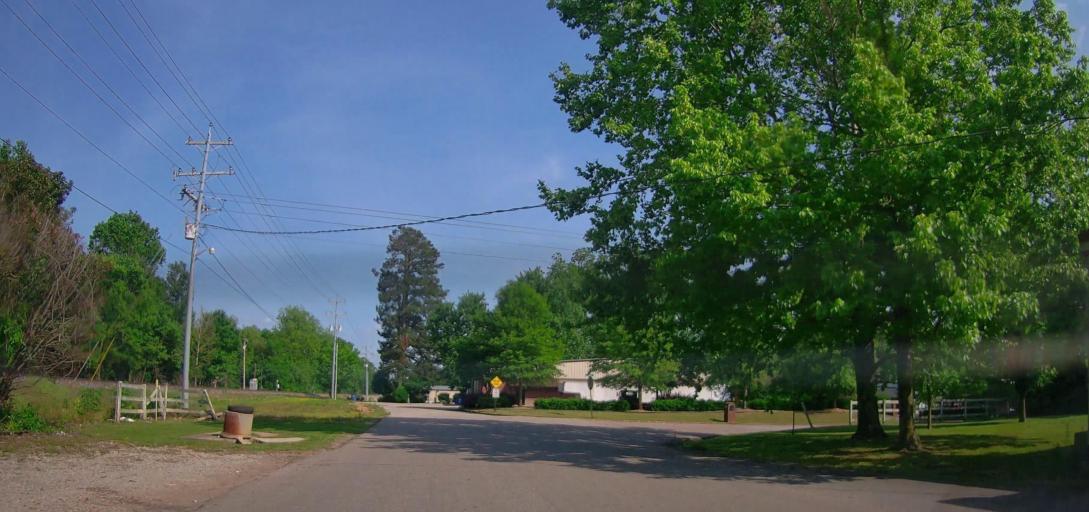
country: US
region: Mississippi
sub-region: De Soto County
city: Olive Branch
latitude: 34.9903
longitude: -89.8611
